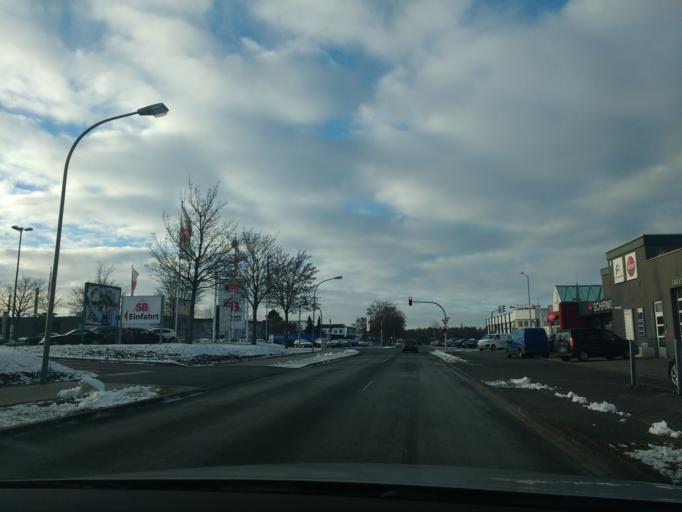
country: DE
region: North Rhine-Westphalia
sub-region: Regierungsbezirk Detmold
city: Paderborn
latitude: 51.7349
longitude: 8.7815
